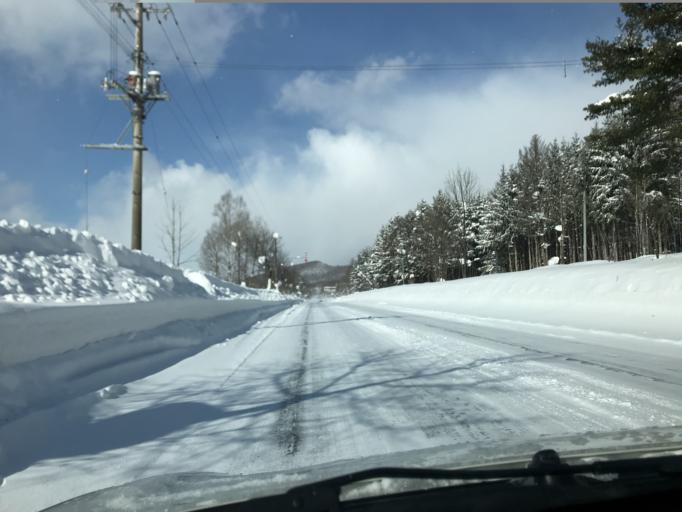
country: JP
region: Hokkaido
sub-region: Asahikawa-shi
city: Asahikawa
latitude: 43.9292
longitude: 142.4730
